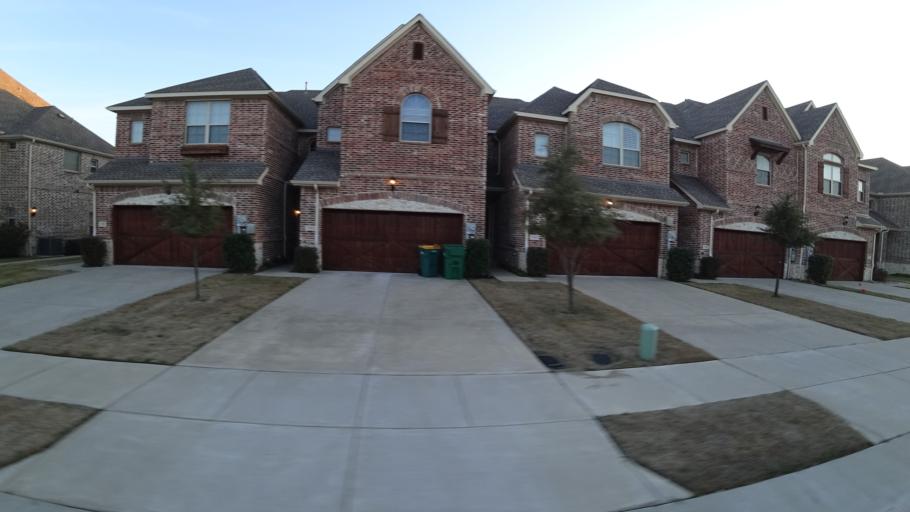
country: US
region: Texas
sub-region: Dallas County
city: Coppell
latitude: 32.9909
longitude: -96.9921
